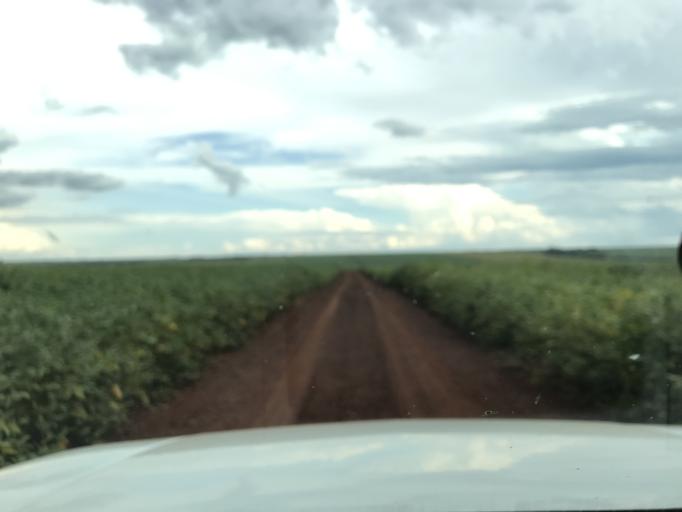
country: BR
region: Parana
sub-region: Palotina
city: Palotina
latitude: -24.2741
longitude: -53.7650
